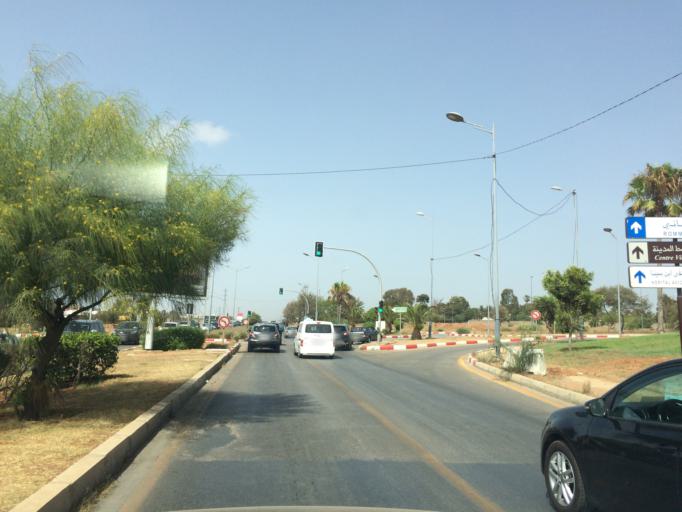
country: MA
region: Rabat-Sale-Zemmour-Zaer
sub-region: Rabat
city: Rabat
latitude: 33.9757
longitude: -6.8623
